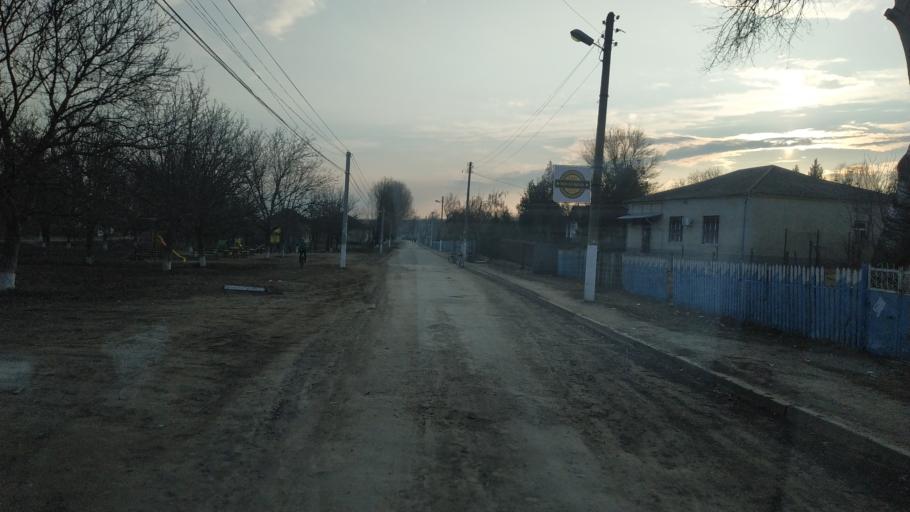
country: MD
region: Hincesti
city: Dancu
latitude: 46.7136
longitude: 28.3482
